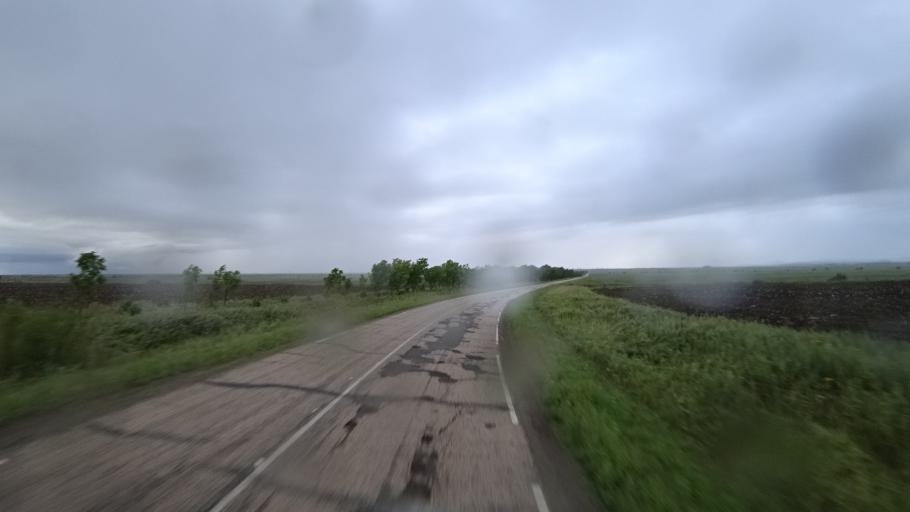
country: RU
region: Primorskiy
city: Chernigovka
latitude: 44.3715
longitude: 132.5301
